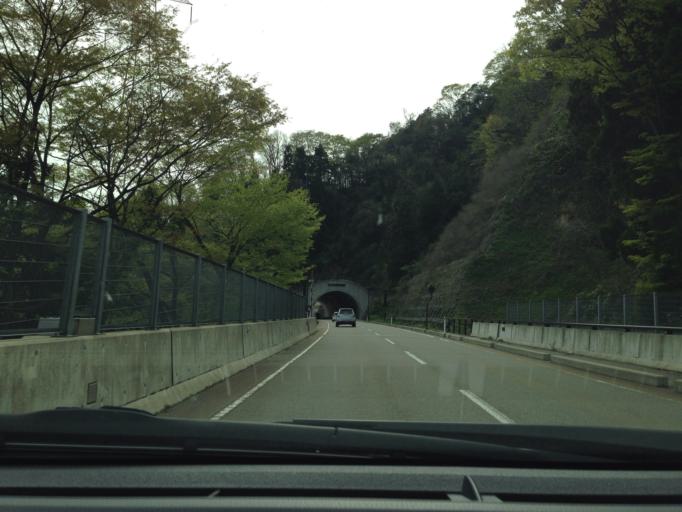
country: JP
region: Toyama
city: Fukumitsu
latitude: 36.5648
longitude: 136.7834
